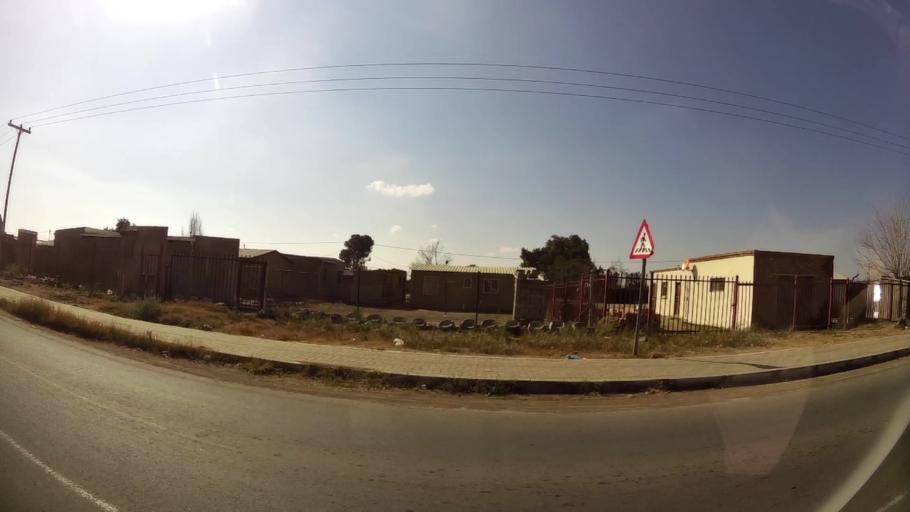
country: ZA
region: Orange Free State
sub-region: Mangaung Metropolitan Municipality
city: Bloemfontein
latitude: -29.1608
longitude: 26.2785
